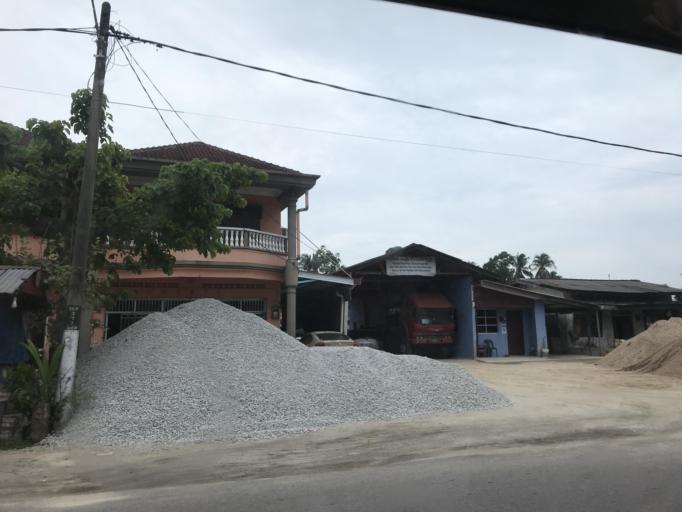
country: MY
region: Kelantan
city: Kota Bharu
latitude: 6.1444
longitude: 102.2268
